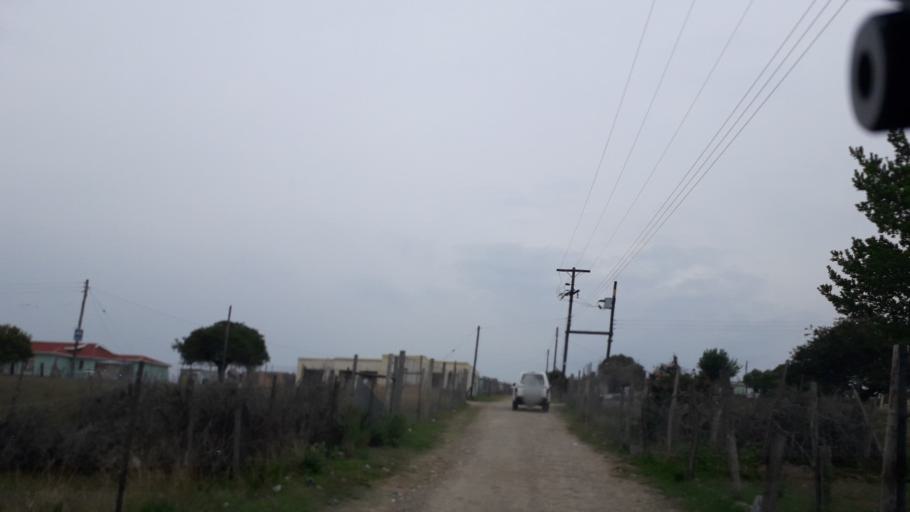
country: ZA
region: Eastern Cape
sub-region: Buffalo City Metropolitan Municipality
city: Bhisho
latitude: -32.8360
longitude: 27.3689
